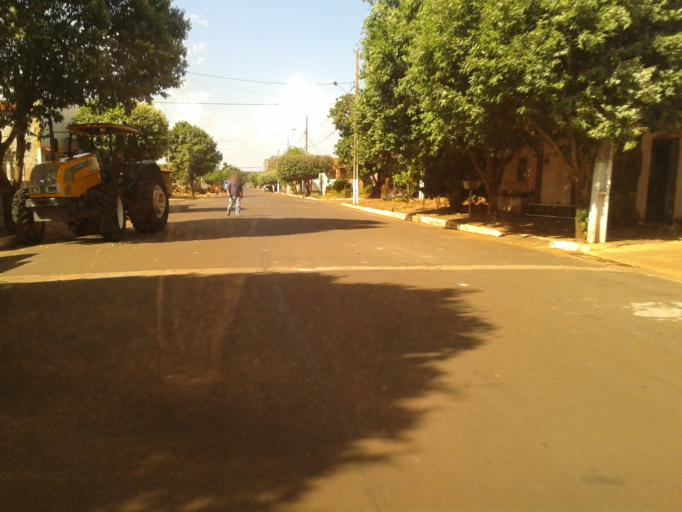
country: BR
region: Minas Gerais
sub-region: Santa Vitoria
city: Santa Vitoria
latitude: -18.6949
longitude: -49.9461
